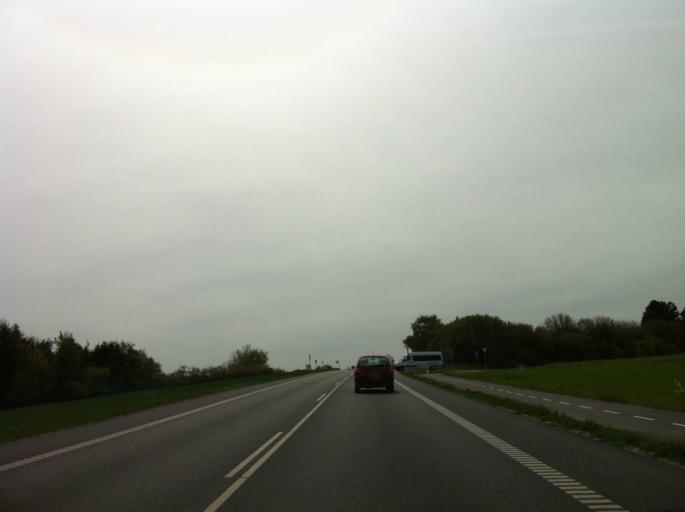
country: DK
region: Capital Region
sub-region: Egedal Kommune
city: Olstykke
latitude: 55.8250
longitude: 12.1641
